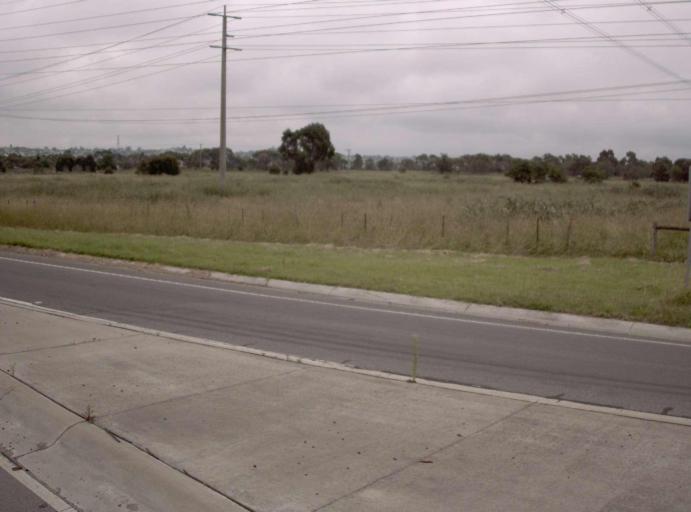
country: AU
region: Victoria
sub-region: Latrobe
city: Morwell
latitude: -38.2485
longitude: 146.4355
